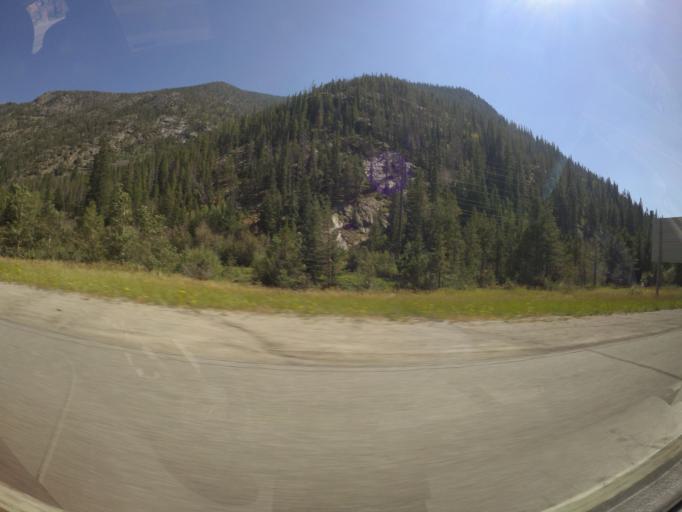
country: US
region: Colorado
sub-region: Summit County
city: Frisco
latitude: 39.5654
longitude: -106.1272
